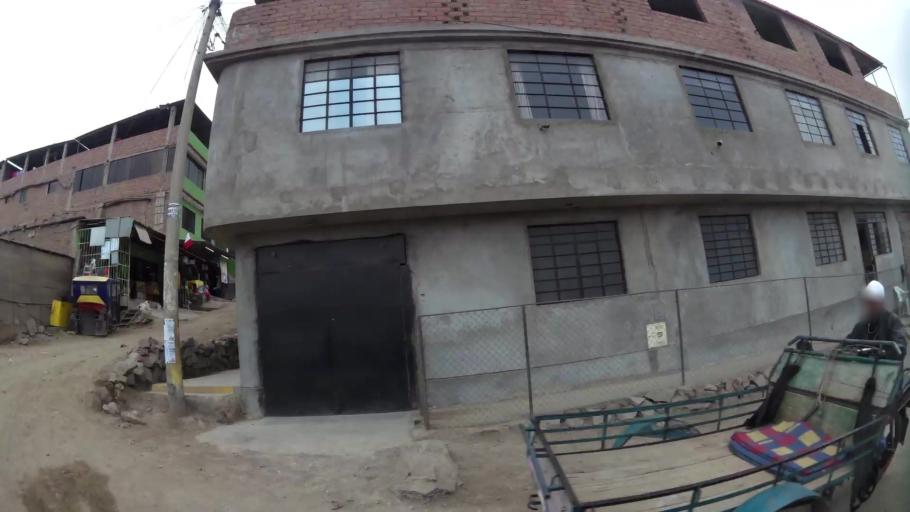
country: PE
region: Lima
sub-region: Lima
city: Surco
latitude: -12.1883
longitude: -76.9490
